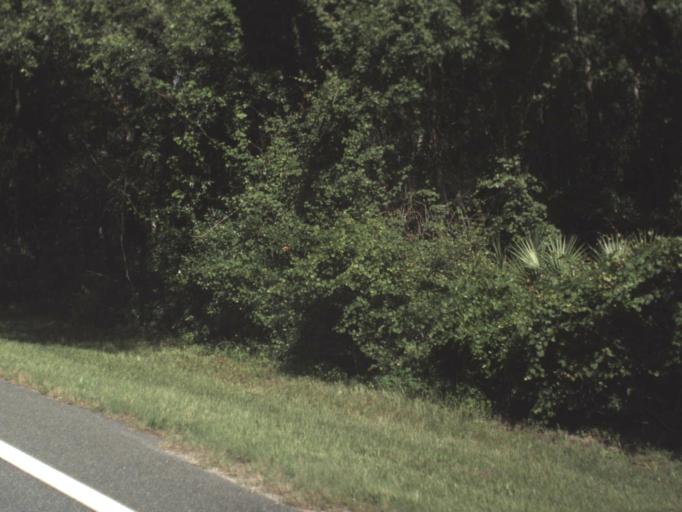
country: US
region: Florida
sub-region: Putnam County
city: Palatka
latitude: 29.5677
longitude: -81.6481
